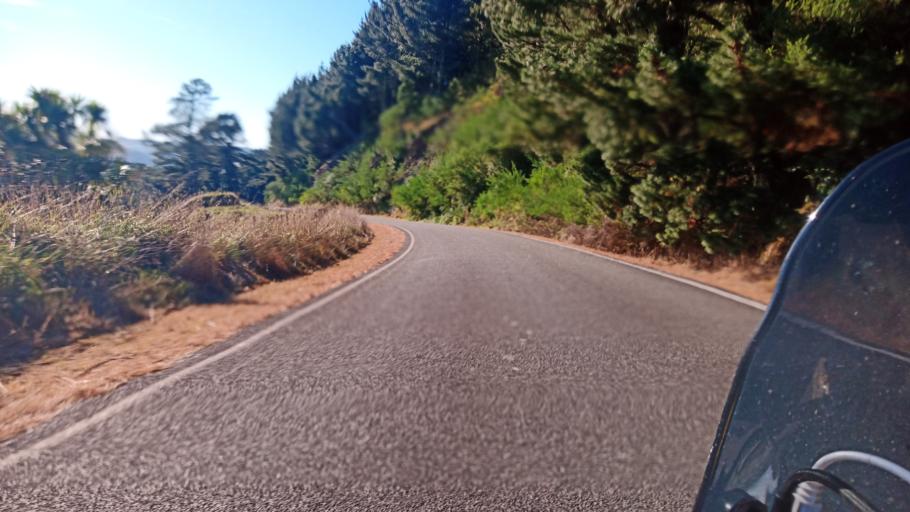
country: NZ
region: Hawke's Bay
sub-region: Wairoa District
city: Wairoa
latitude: -38.8307
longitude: 177.2863
